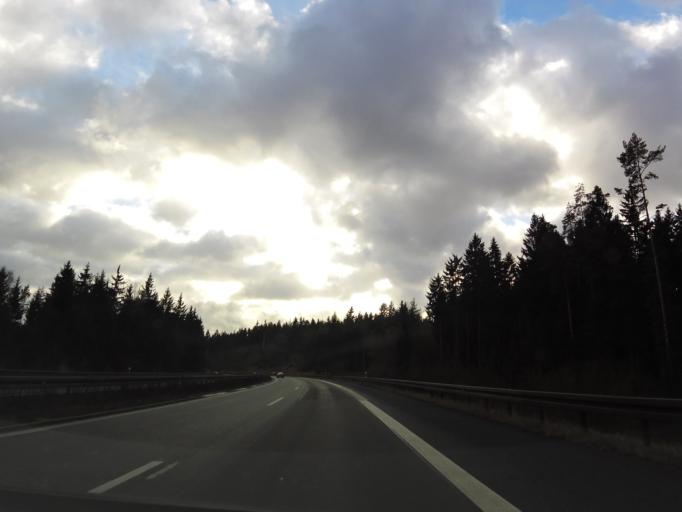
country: DE
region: Bavaria
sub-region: Upper Franconia
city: Thierstein
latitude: 50.1461
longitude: 12.0846
